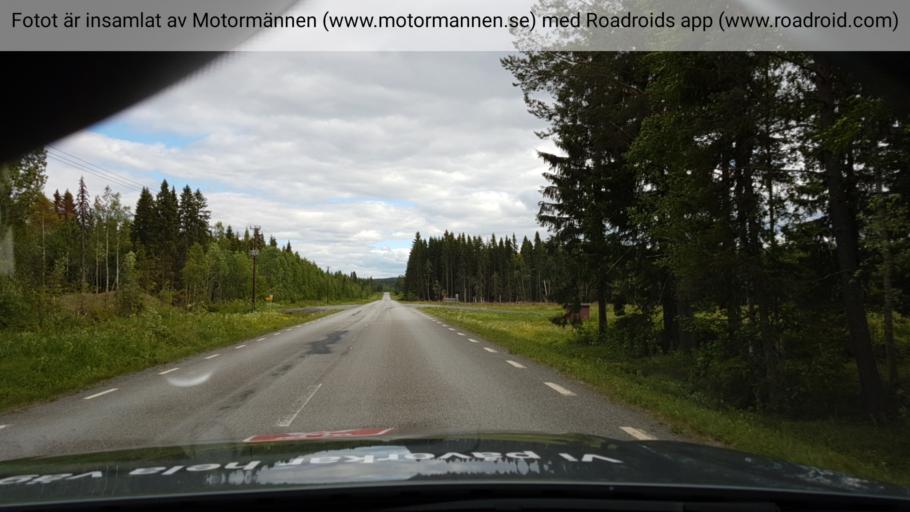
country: SE
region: Jaemtland
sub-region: Stroemsunds Kommun
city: Stroemsund
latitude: 63.9317
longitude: 15.4996
